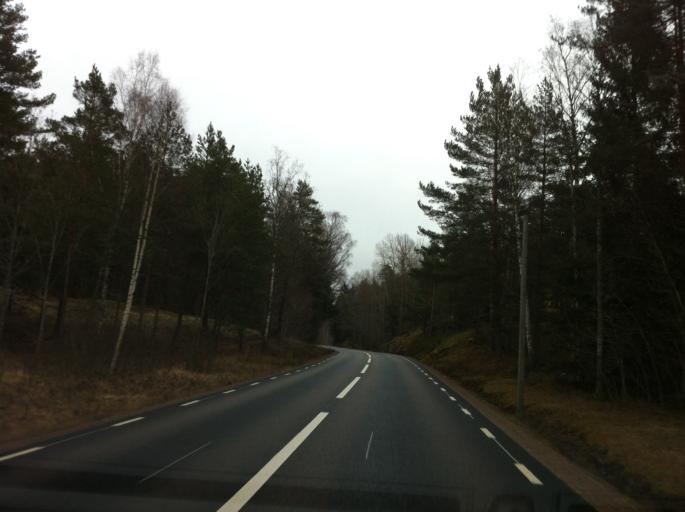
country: SE
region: Kalmar
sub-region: Vasterviks Kommun
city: Overum
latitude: 57.9092
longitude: 16.2026
